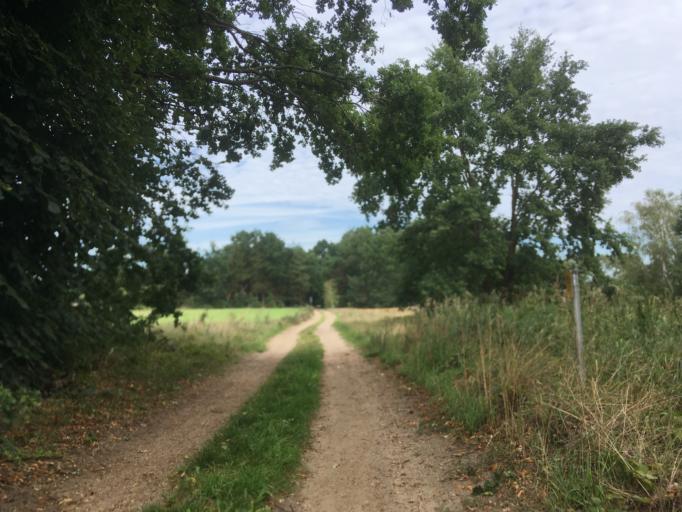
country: DE
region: Brandenburg
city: Wandlitz
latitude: 52.7622
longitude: 13.4170
